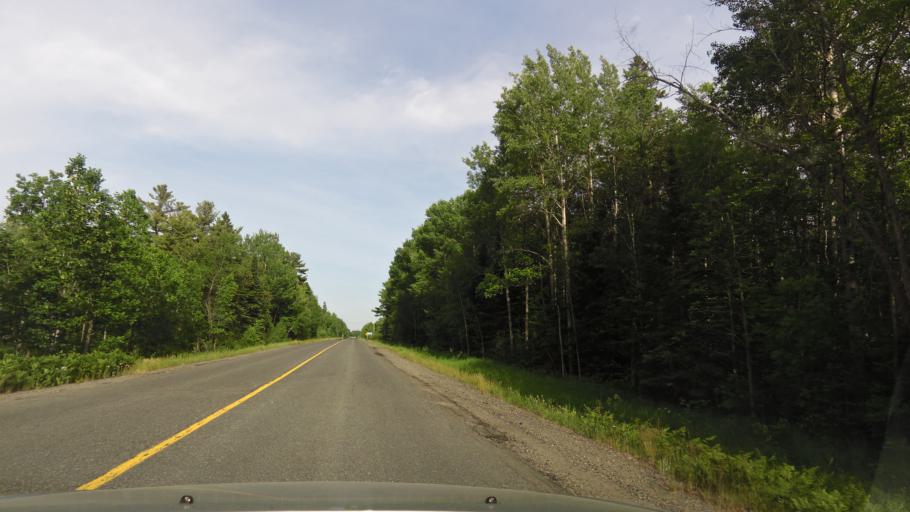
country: CA
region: Ontario
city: Greater Sudbury
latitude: 45.9131
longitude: -80.5653
